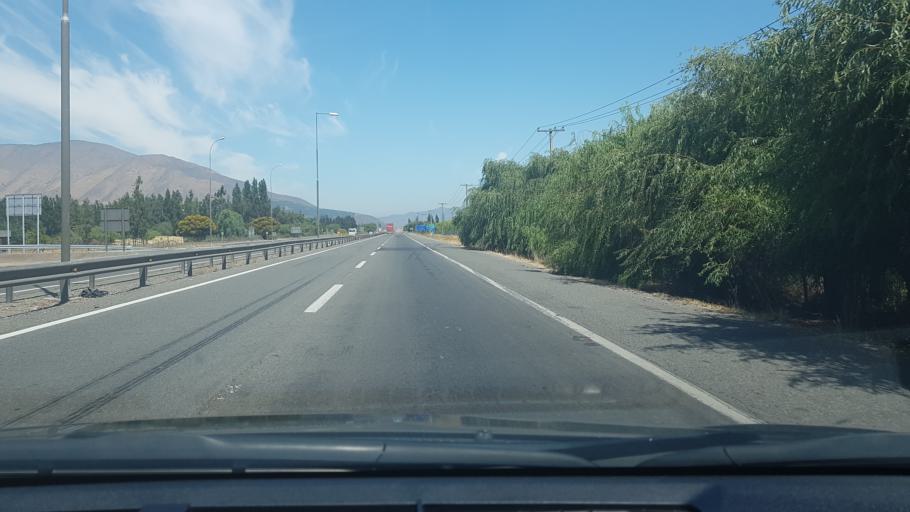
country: CL
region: Valparaiso
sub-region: Provincia de San Felipe
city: Llaillay
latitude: -32.8504
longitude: -70.9466
